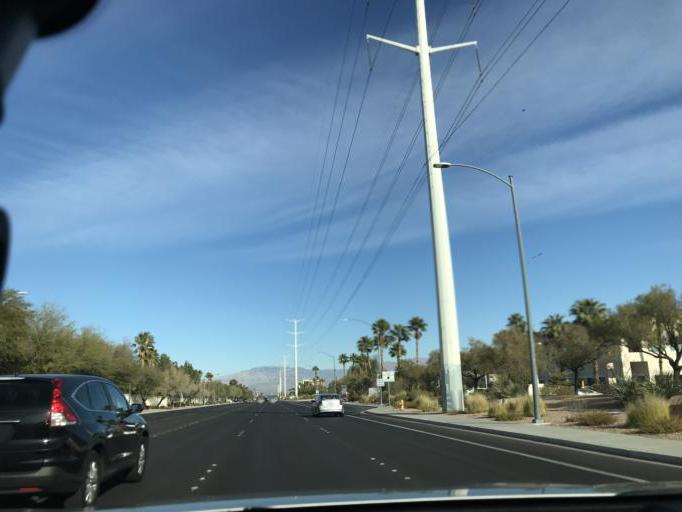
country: US
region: Nevada
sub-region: Clark County
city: Spring Valley
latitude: 36.2047
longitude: -115.2606
